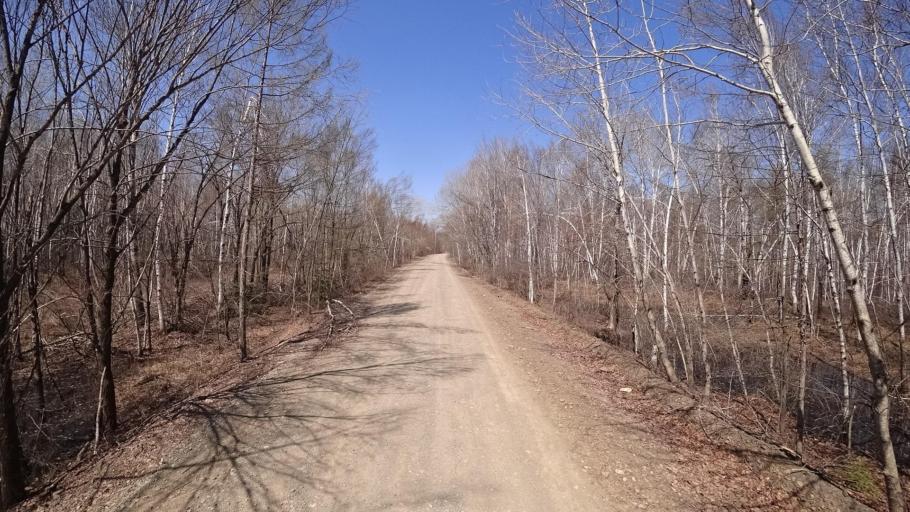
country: RU
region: Khabarovsk Krai
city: Khurba
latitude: 50.4153
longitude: 136.8393
